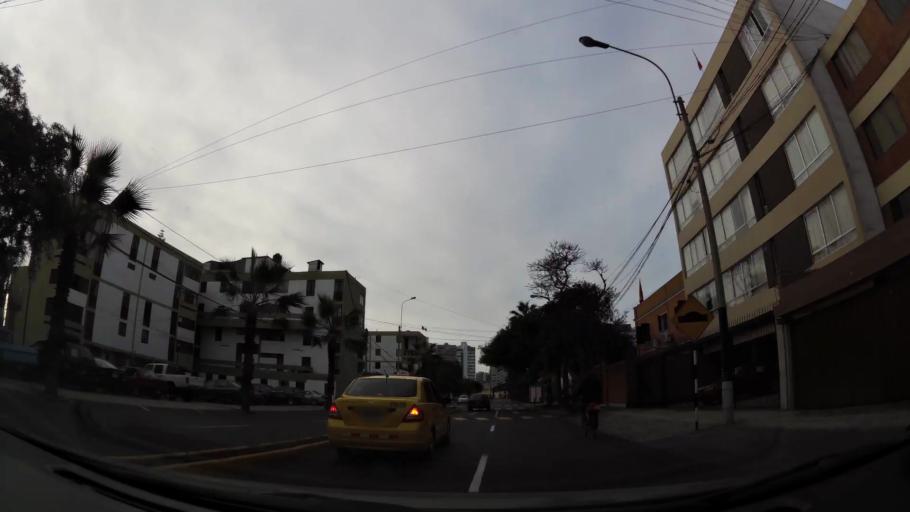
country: PE
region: Lima
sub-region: Lima
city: San Isidro
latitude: -12.1070
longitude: -77.0477
